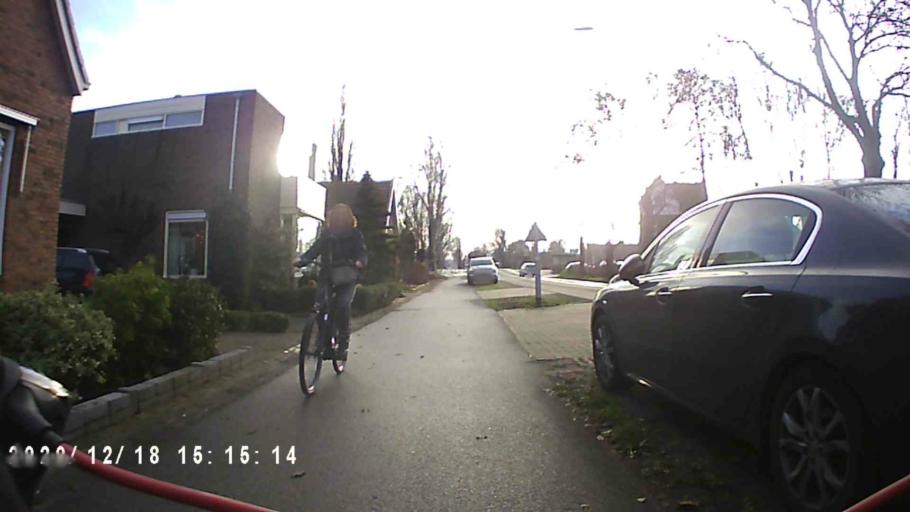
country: NL
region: Groningen
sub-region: Gemeente Hoogezand-Sappemeer
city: Hoogezand
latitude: 53.1624
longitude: 6.7227
